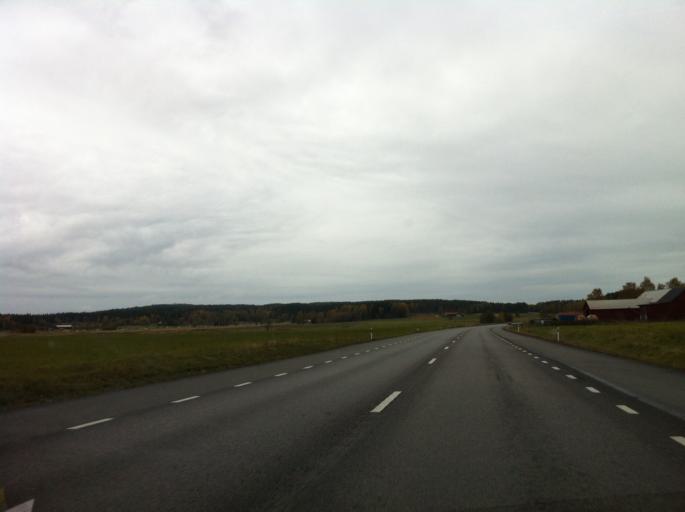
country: SE
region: OErebro
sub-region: Lindesbergs Kommun
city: Stora
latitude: 59.7534
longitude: 15.1447
